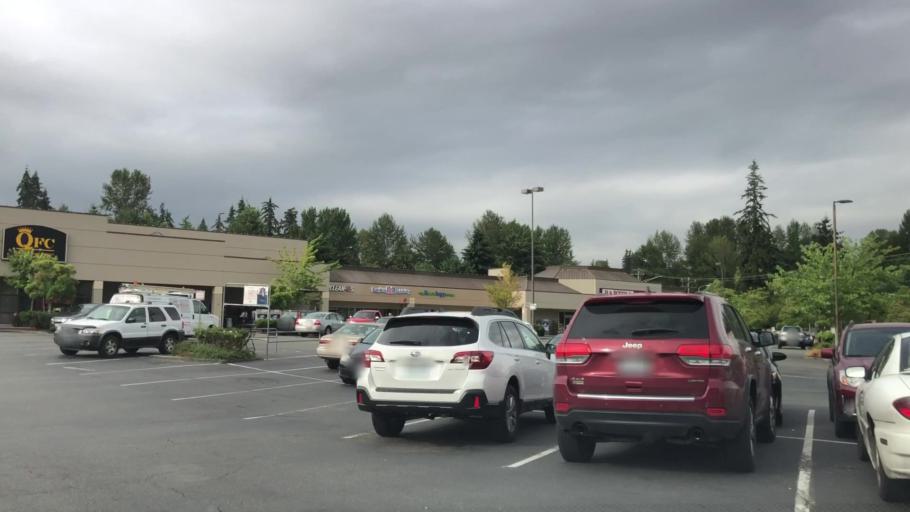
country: US
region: Washington
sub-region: King County
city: Bothell
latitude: 47.7905
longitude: -122.2161
